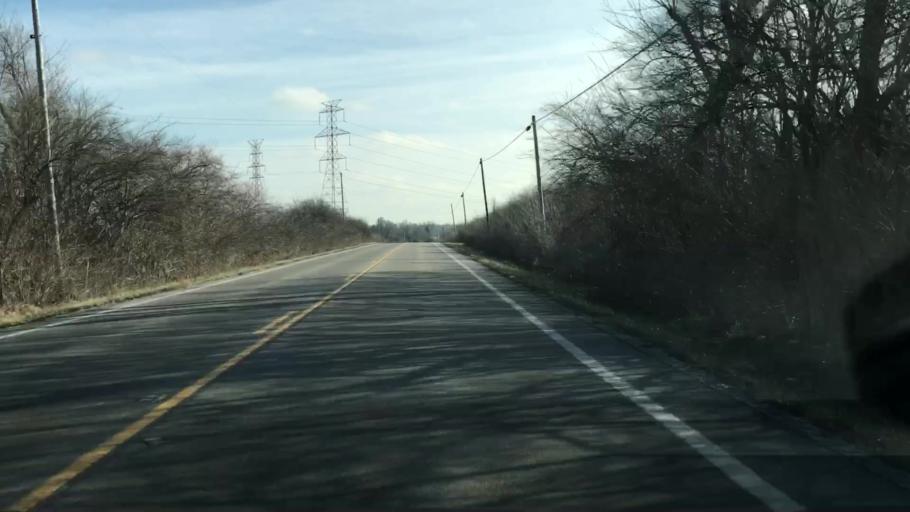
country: US
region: Ohio
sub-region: Greene County
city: Fairborn
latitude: 39.8059
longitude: -83.9756
